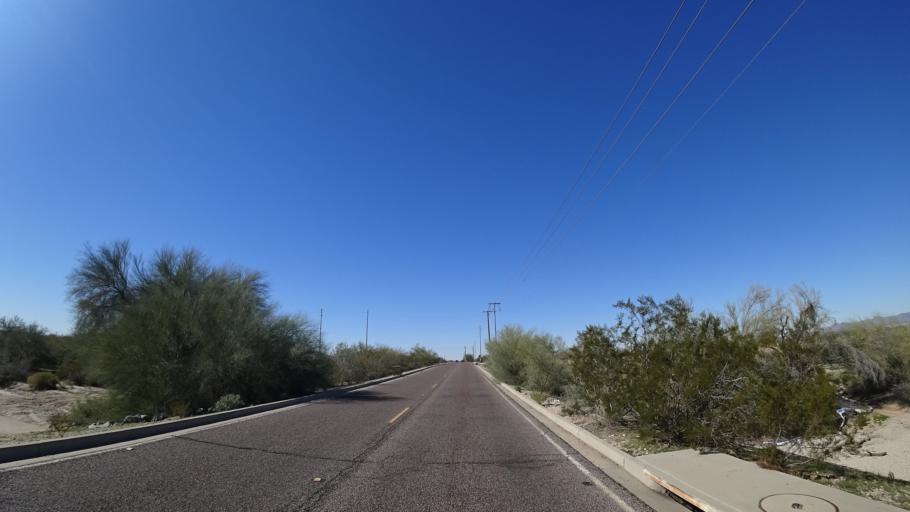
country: US
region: Arizona
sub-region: Maricopa County
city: Buckeye
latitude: 33.3485
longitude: -112.4666
